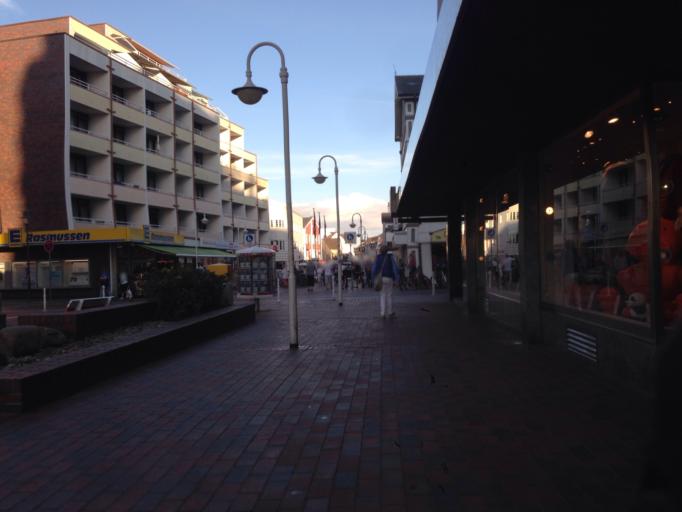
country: DE
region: Schleswig-Holstein
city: Westerland
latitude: 54.9092
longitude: 8.3011
